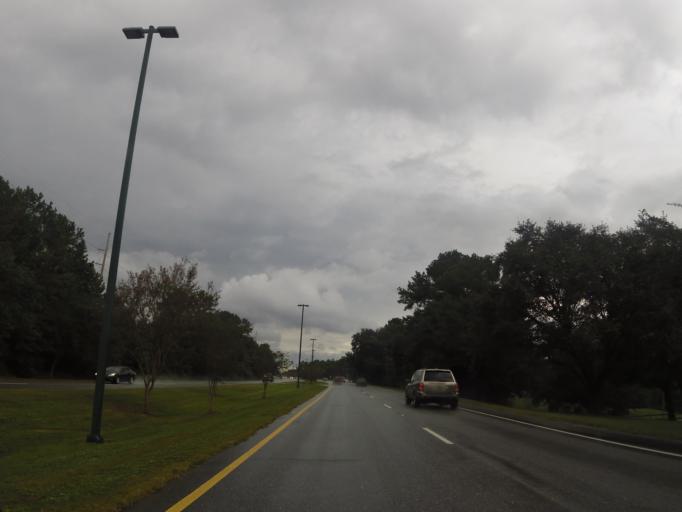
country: US
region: Alabama
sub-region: Baldwin County
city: Daphne
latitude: 30.5651
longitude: -87.8941
